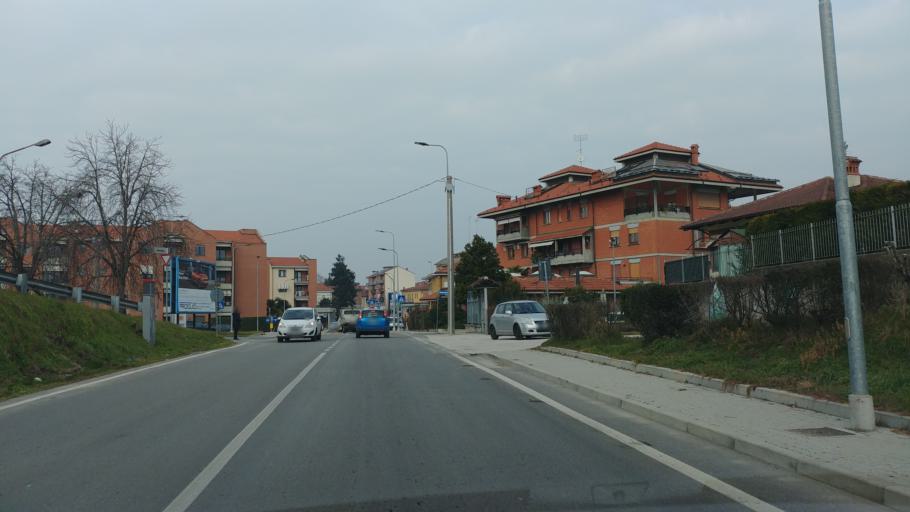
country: IT
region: Piedmont
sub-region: Provincia di Cuneo
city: Fossano
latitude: 44.5425
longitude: 7.7214
